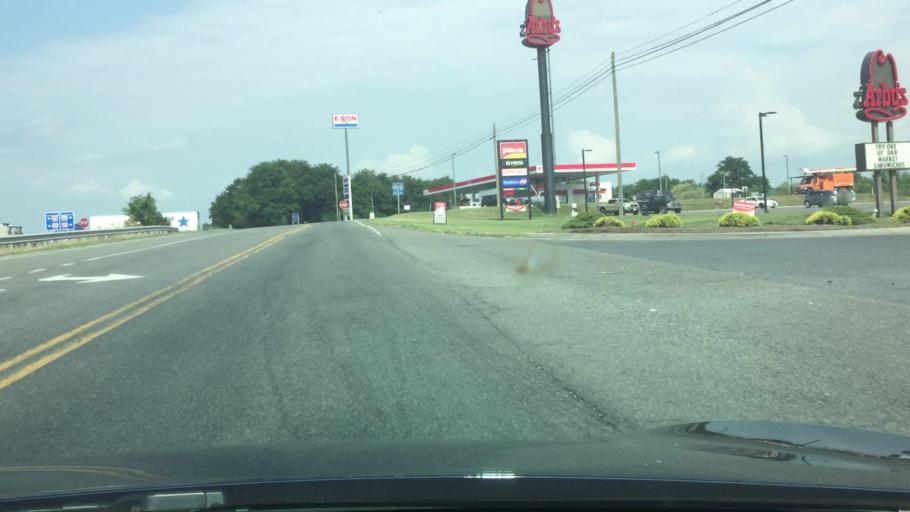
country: US
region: Virginia
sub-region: Wythe County
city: Wytheville
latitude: 36.9378
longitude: -80.9926
